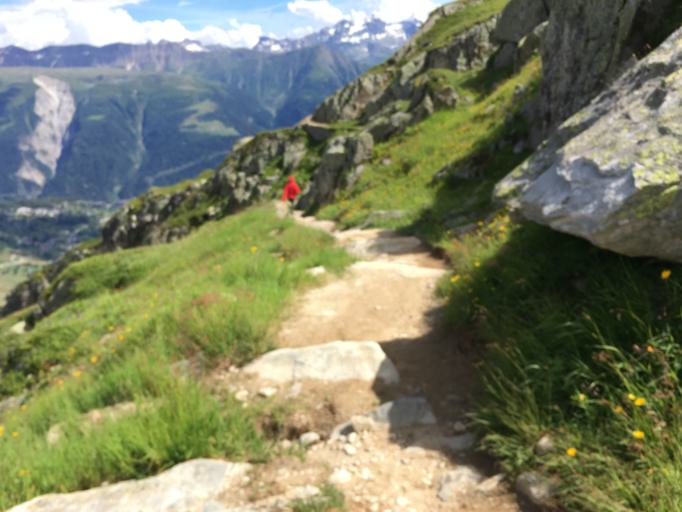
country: CH
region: Valais
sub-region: Goms District
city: Fiesch
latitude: 46.4442
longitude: 8.1194
